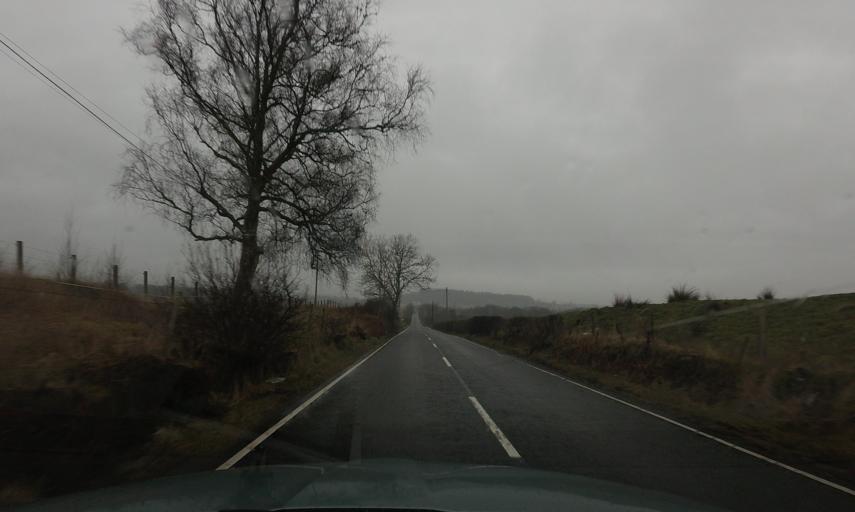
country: GB
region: Scotland
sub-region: Stirling
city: Balfron
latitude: 56.1237
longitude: -4.3592
